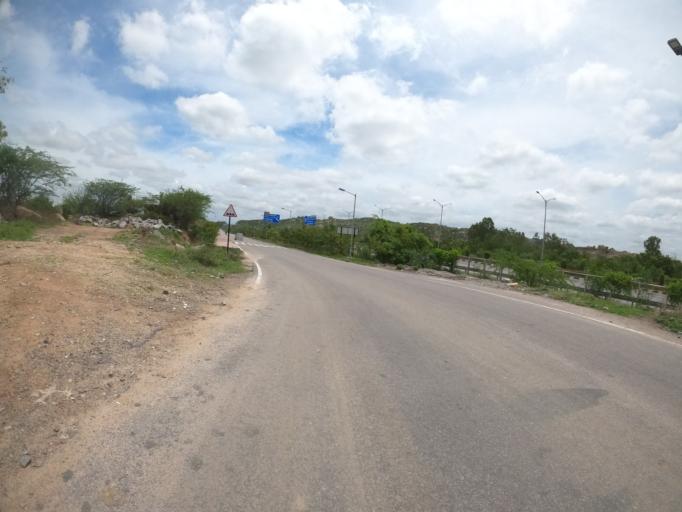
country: IN
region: Telangana
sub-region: Hyderabad
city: Hyderabad
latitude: 17.2999
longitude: 78.3789
